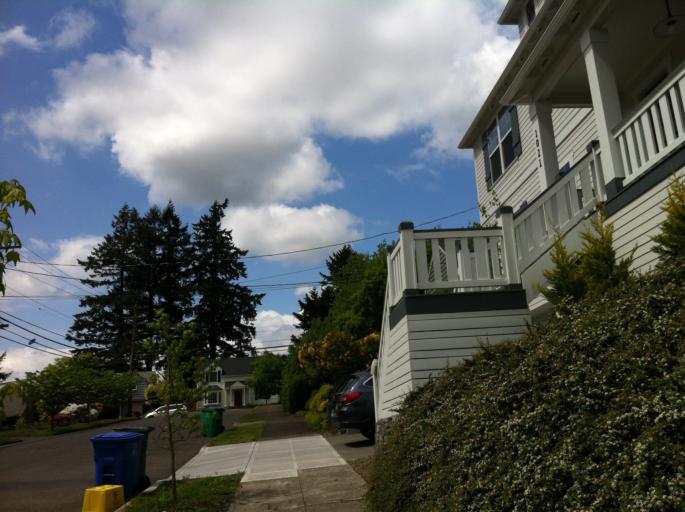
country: US
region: Oregon
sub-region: Clackamas County
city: Lake Oswego
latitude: 45.4643
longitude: -122.6890
